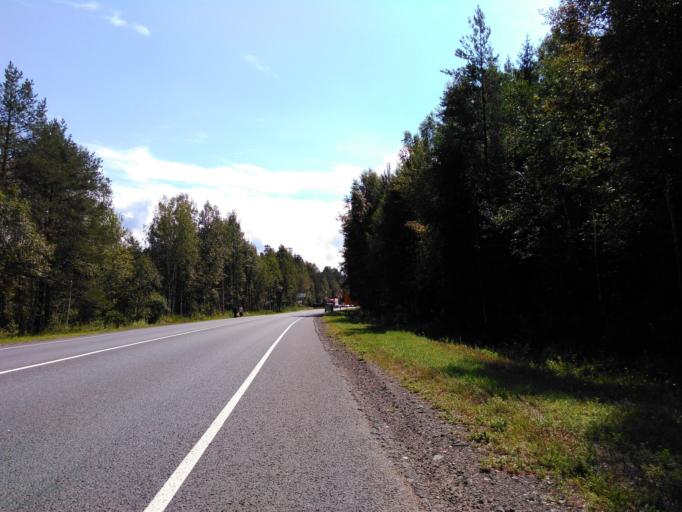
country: RU
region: Moskovskaya
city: Elektrogorsk
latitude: 56.0247
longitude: 38.7594
